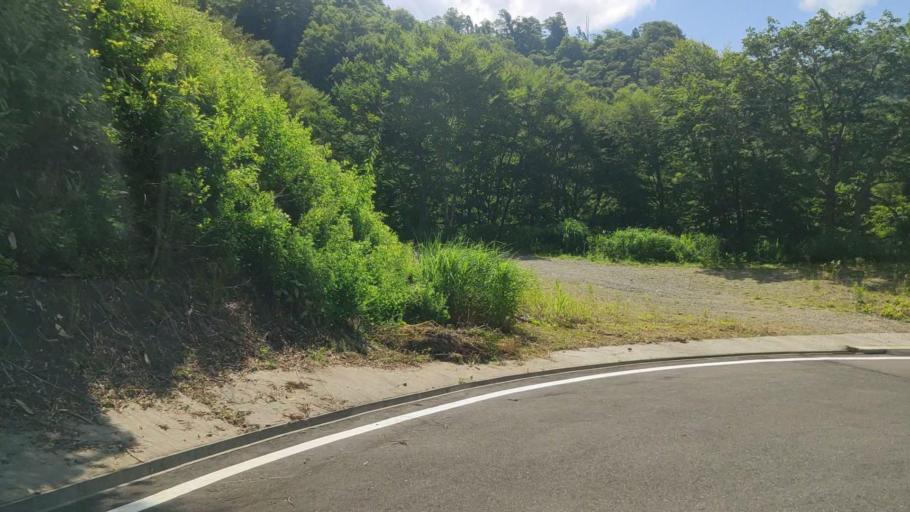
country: JP
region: Fukui
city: Katsuyama
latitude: 36.1463
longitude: 136.5210
